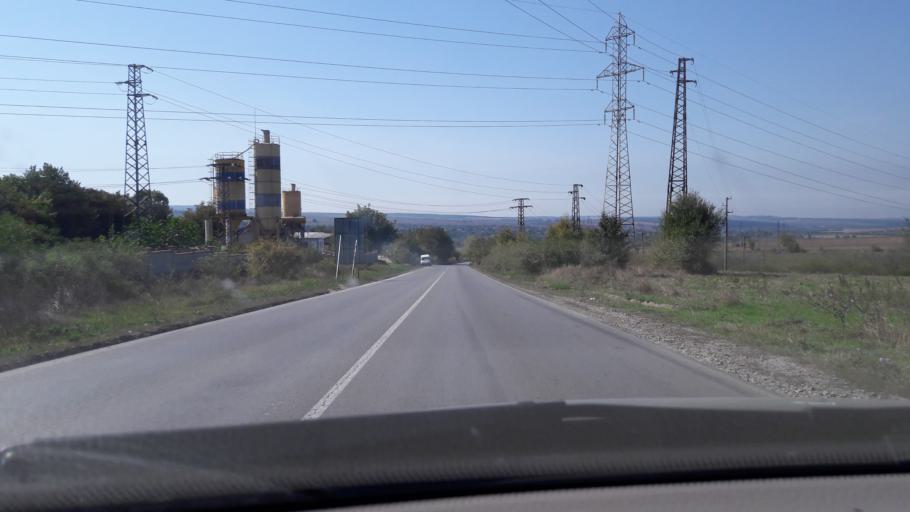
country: BG
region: Razgrad
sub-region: Obshtina Razgrad
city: Razgrad
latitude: 43.5445
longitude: 26.5089
